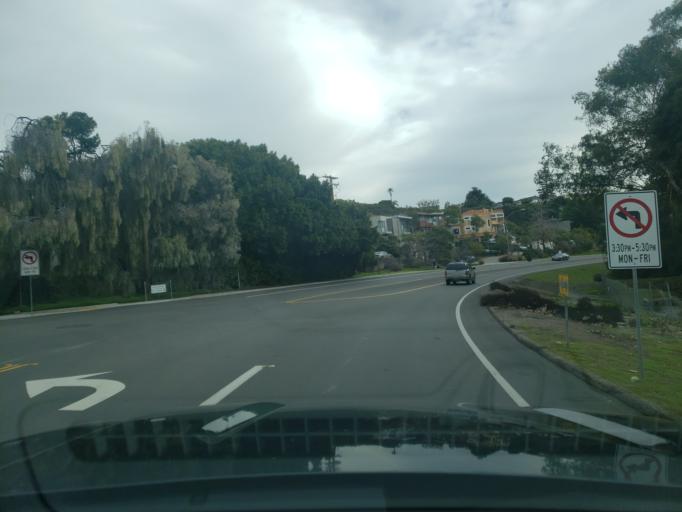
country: US
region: California
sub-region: San Diego County
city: Coronado
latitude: 32.7280
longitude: -117.2400
